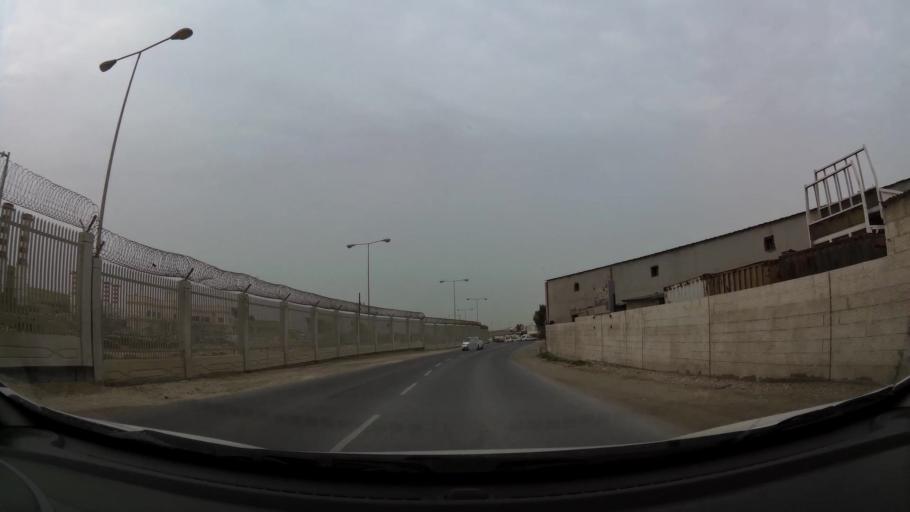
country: BH
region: Northern
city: Ar Rifa'
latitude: 26.1180
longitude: 50.5890
